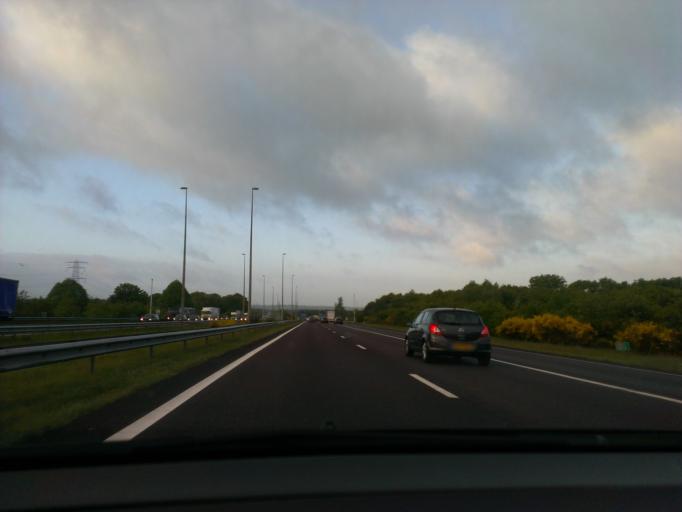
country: NL
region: Gelderland
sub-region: Gemeente Rozendaal
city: Rozendaal
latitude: 52.0619
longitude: 5.9418
